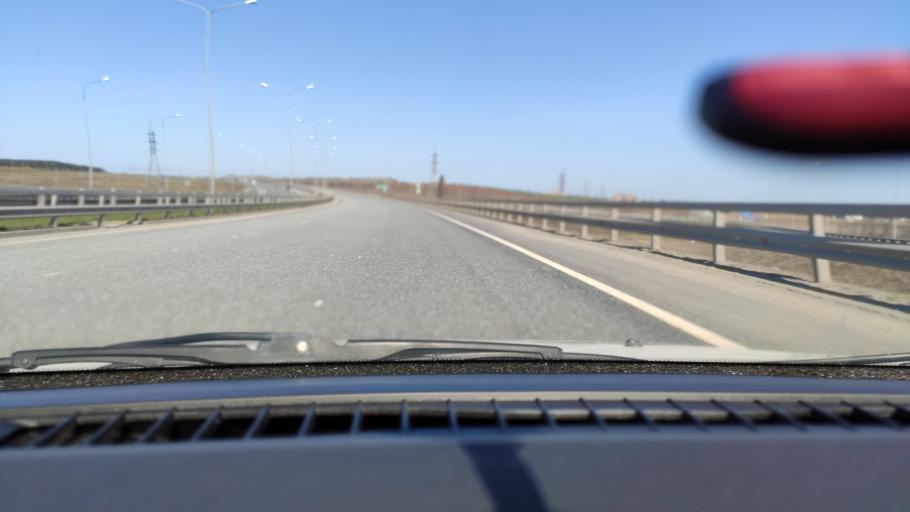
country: RU
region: Perm
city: Lobanovo
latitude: 57.8421
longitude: 56.2965
